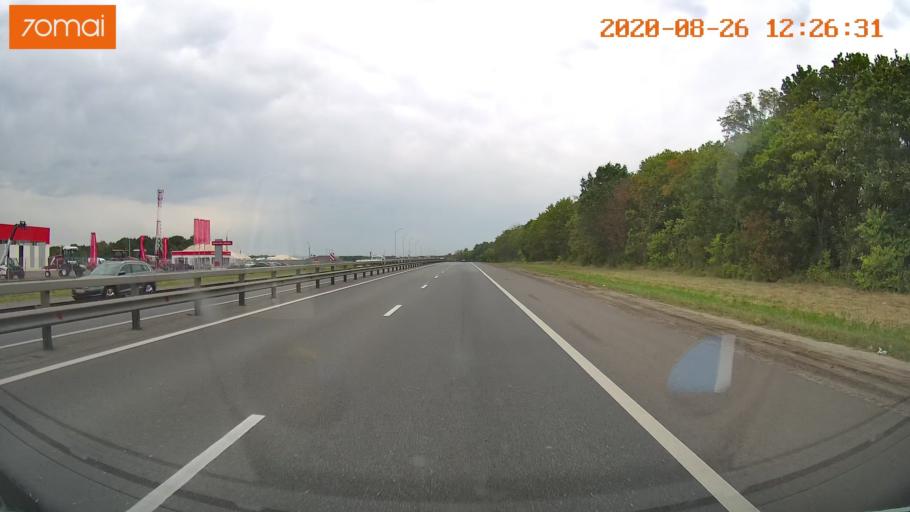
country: RU
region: Rjazan
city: Polyany
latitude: 54.5358
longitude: 39.8586
